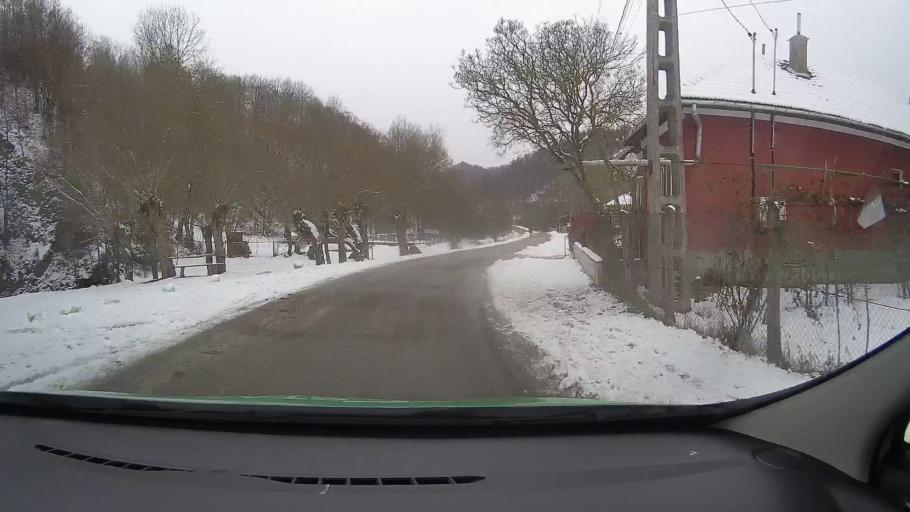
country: RO
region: Hunedoara
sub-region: Comuna Balsa
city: Balsa
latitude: 46.0557
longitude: 23.0840
